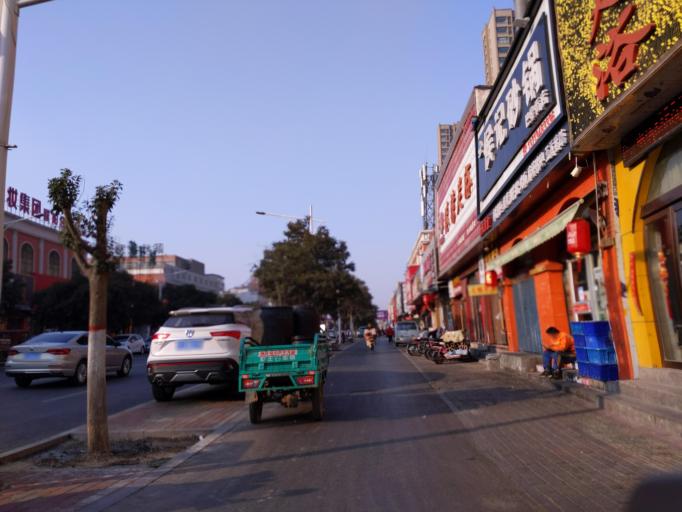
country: CN
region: Henan Sheng
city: Puyang
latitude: 35.7749
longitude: 115.0329
